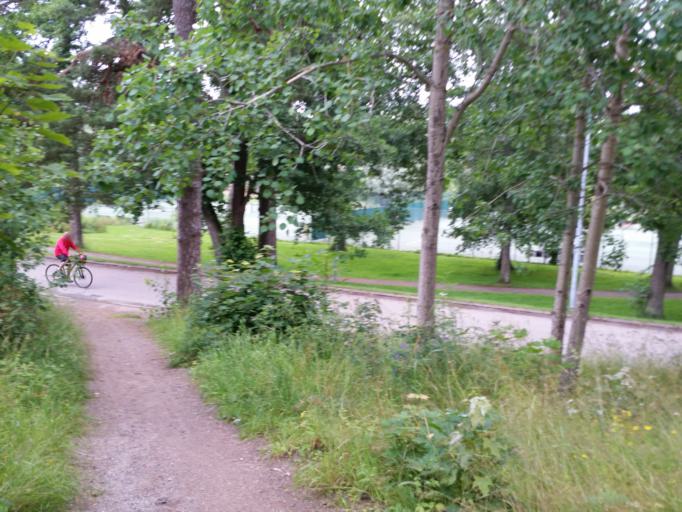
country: FI
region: Uusimaa
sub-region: Raaseporin
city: Hanko
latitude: 59.8244
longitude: 22.9743
